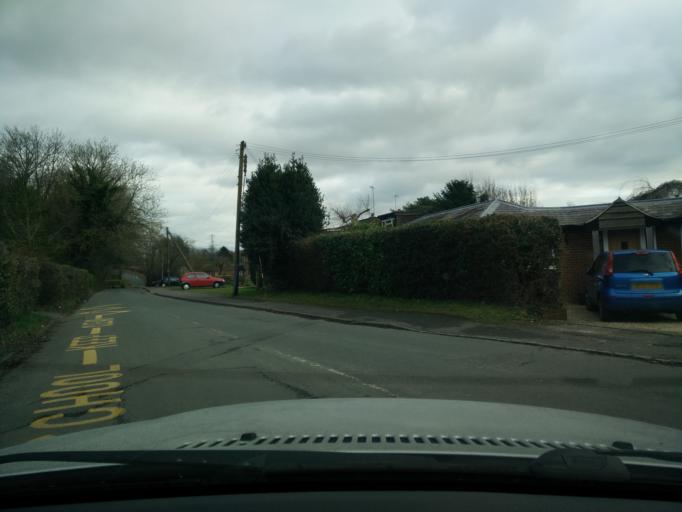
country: GB
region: England
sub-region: Buckinghamshire
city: Amersham
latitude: 51.6585
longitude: -0.6643
